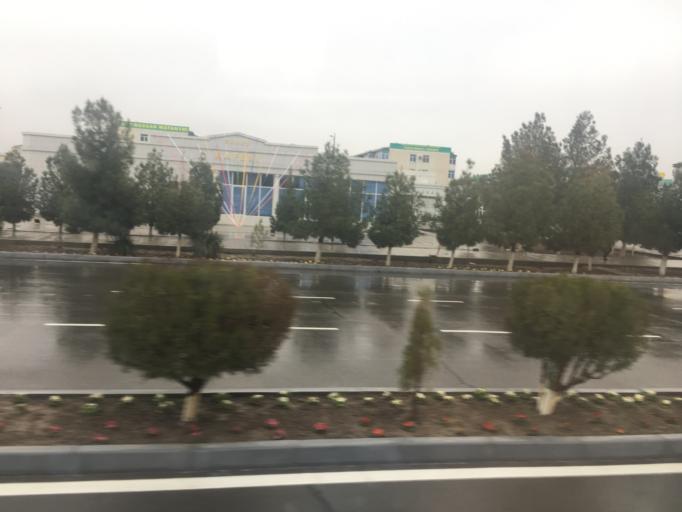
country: TM
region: Lebap
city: Turkmenabat
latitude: 39.0778
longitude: 63.5865
